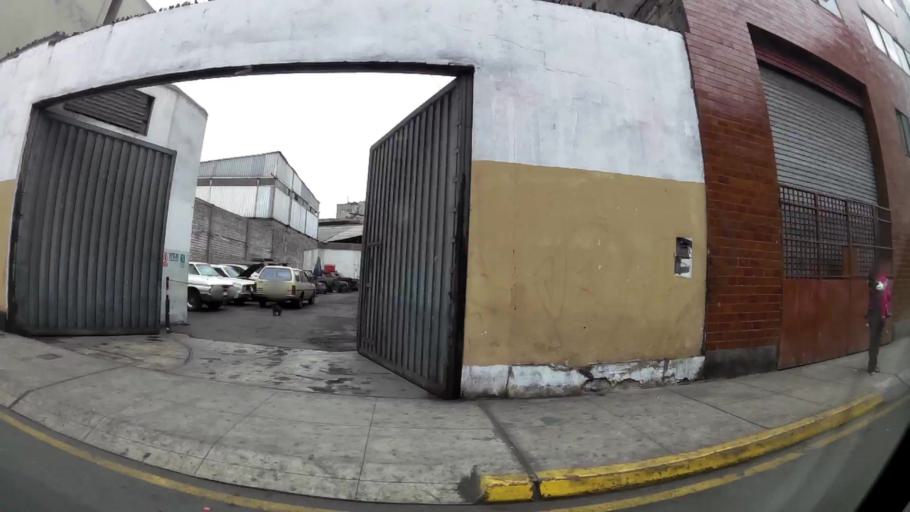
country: PE
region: Lima
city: Lima
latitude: -12.0508
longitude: -77.0408
